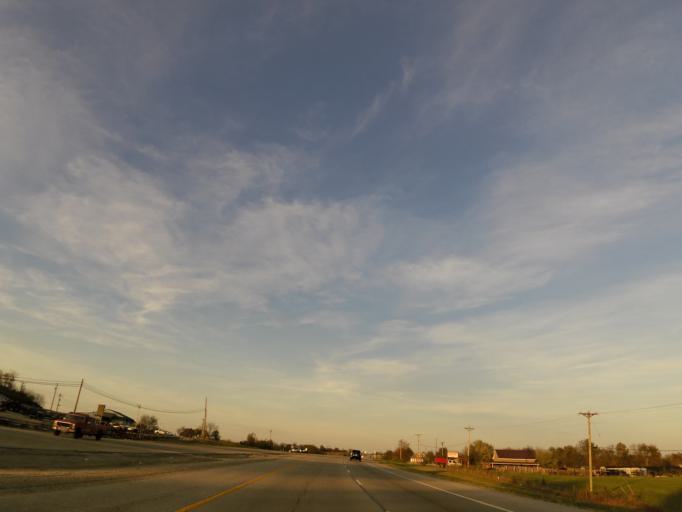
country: US
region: Kentucky
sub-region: Jessamine County
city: Nicholasville
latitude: 37.8200
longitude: -84.5964
